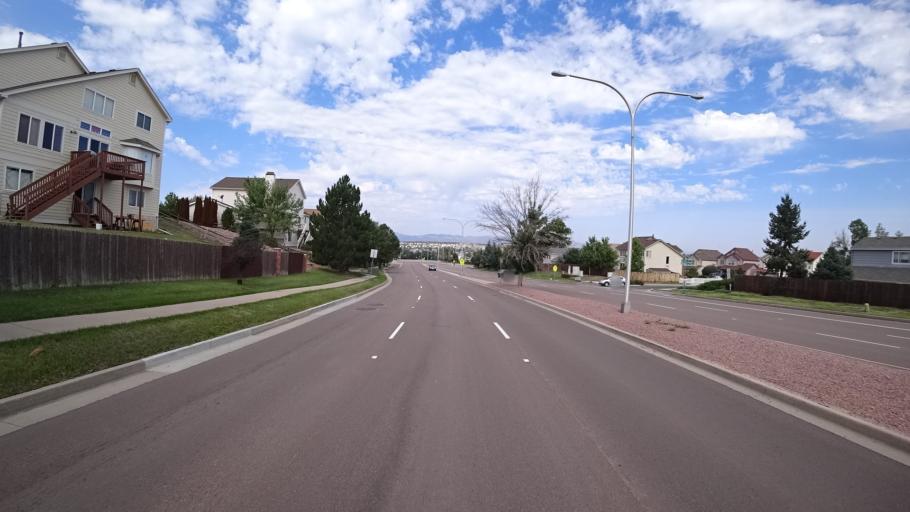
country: US
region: Colorado
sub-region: El Paso County
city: Cimarron Hills
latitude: 38.9025
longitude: -104.6938
